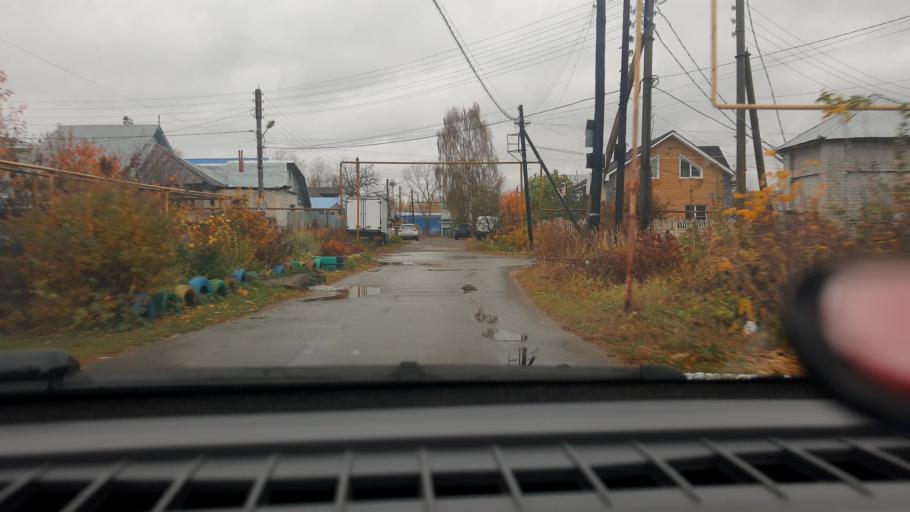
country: RU
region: Nizjnij Novgorod
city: Nizhniy Novgorod
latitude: 56.2972
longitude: 43.9192
